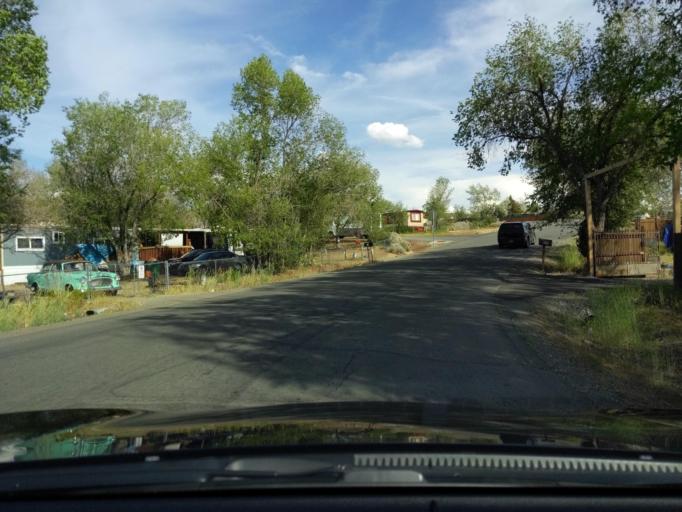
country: US
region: Nevada
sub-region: Washoe County
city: Sun Valley
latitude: 39.5819
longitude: -119.7753
